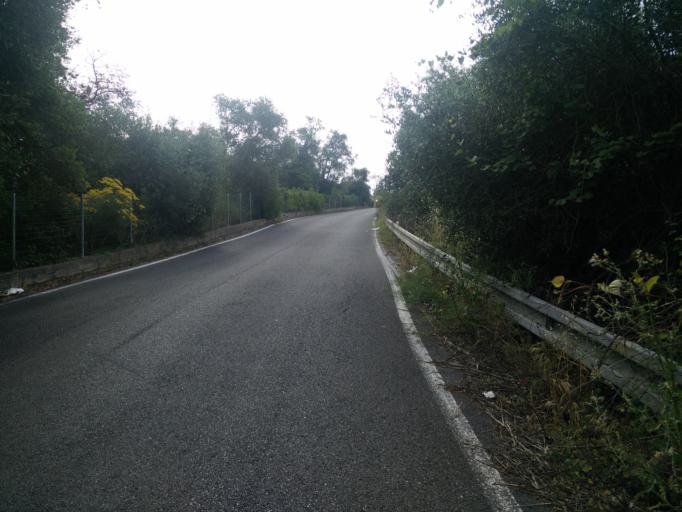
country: IT
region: Liguria
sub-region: Provincia di Imperia
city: Imperia
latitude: 43.8758
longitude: 7.9974
